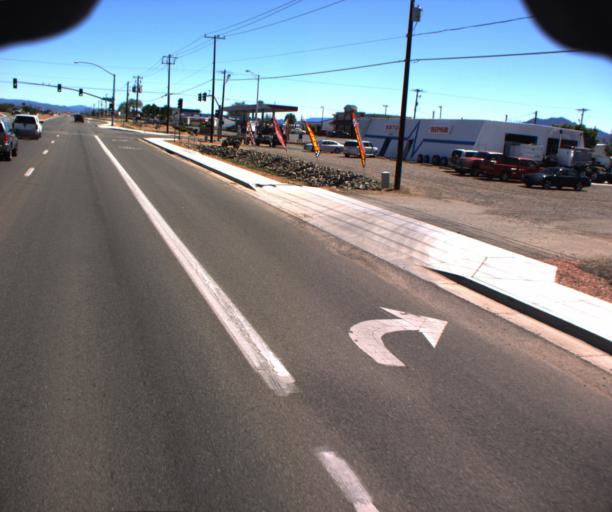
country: US
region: Arizona
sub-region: Yavapai County
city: Chino Valley
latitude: 34.7318
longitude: -112.4542
